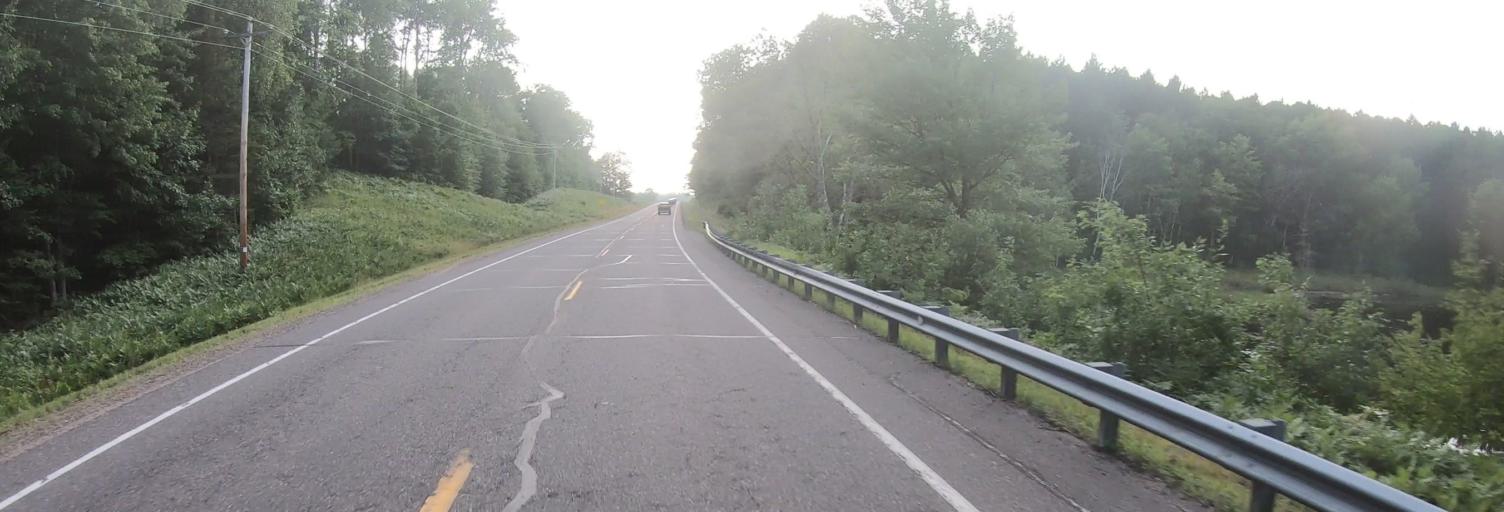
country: US
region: Wisconsin
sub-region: Sawyer County
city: Little Round Lake
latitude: 46.0646
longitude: -91.1451
